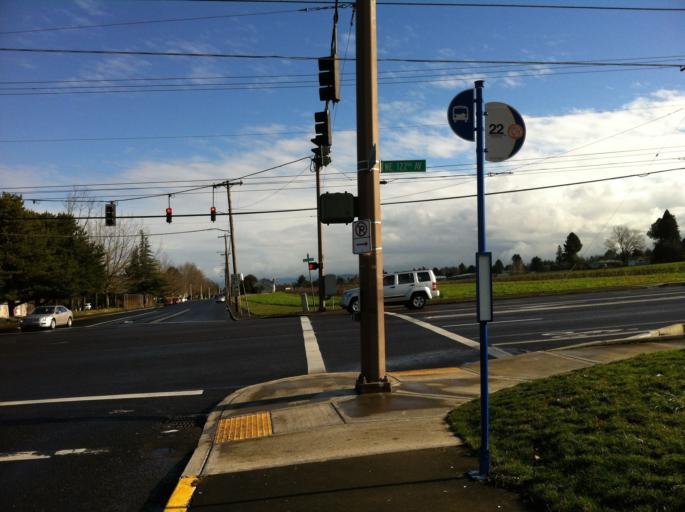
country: US
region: Oregon
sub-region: Multnomah County
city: Lents
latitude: 45.5516
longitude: -122.5375
